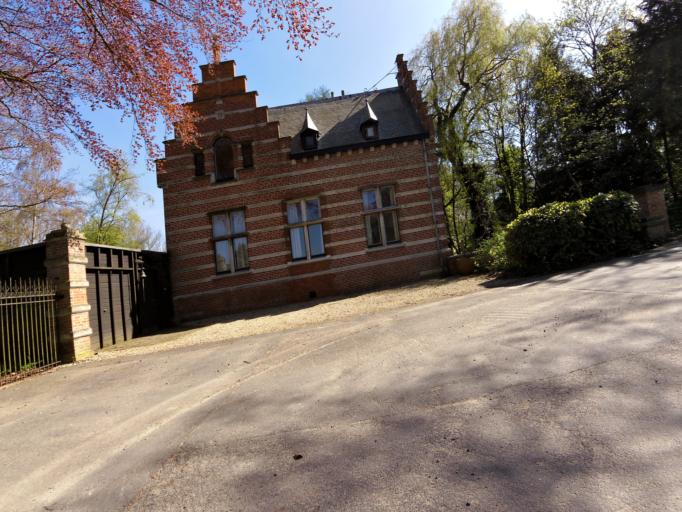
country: BE
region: Flanders
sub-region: Provincie West-Vlaanderen
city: Jabbeke
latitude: 51.1905
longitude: 3.0852
